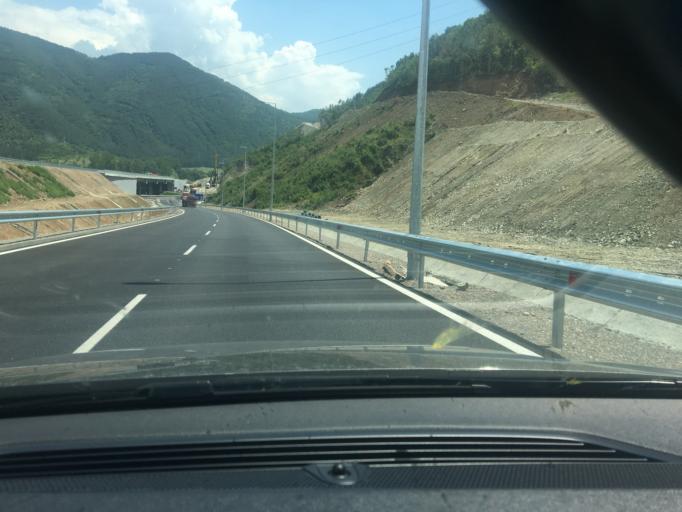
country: BG
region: Blagoevgrad
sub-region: Obshtina Blagoevgrad
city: Blagoevgrad
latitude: 41.9633
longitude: 23.0964
